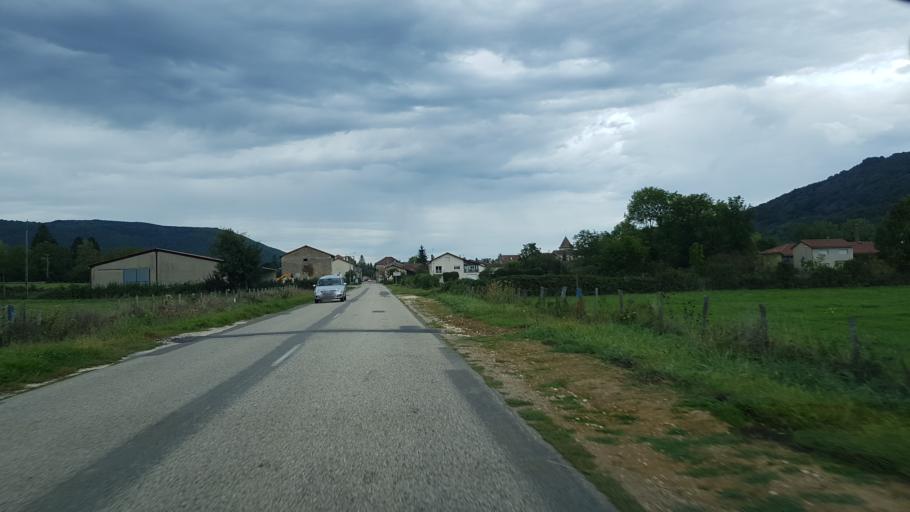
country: FR
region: Rhone-Alpes
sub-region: Departement de l'Ain
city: Cuisiat
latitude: 46.2602
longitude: 5.4253
